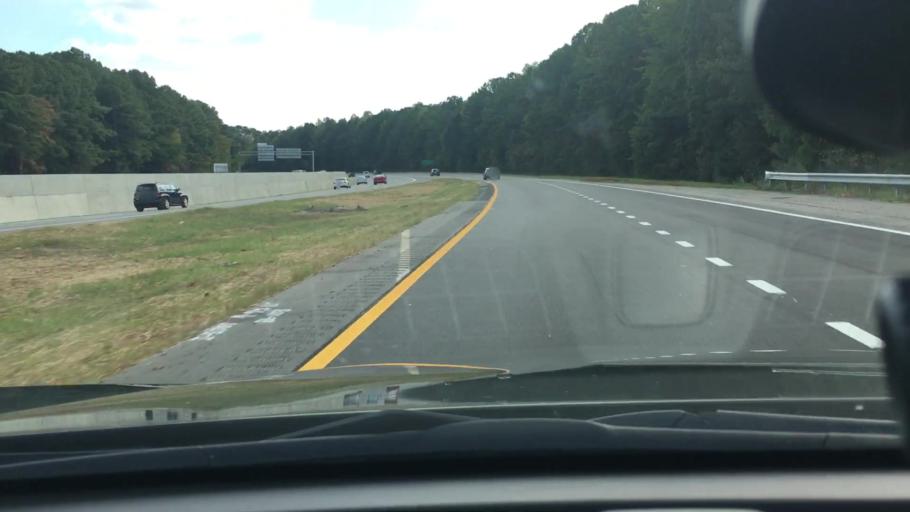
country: US
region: North Carolina
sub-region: Wake County
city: Cary
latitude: 35.7613
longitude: -78.7337
